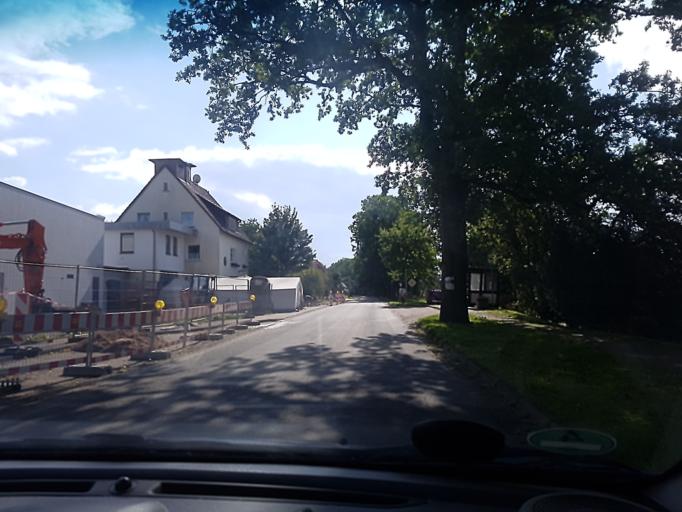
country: DE
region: Lower Saxony
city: Arholzen
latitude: 51.7652
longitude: 9.5430
